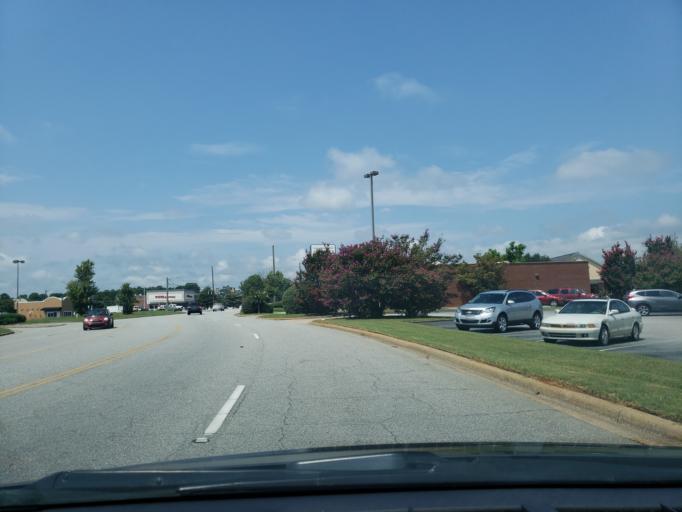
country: US
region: Georgia
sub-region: Dougherty County
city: Albany
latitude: 31.6109
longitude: -84.2212
